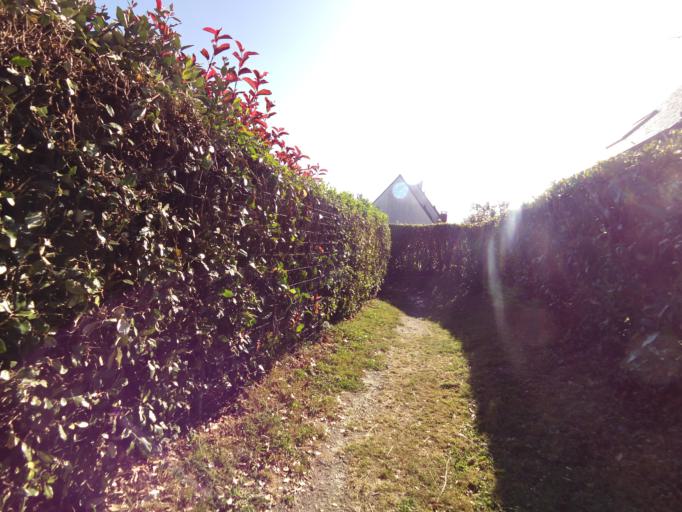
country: FR
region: Brittany
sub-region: Departement du Morbihan
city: Ploermel
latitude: 47.9288
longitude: -2.4064
